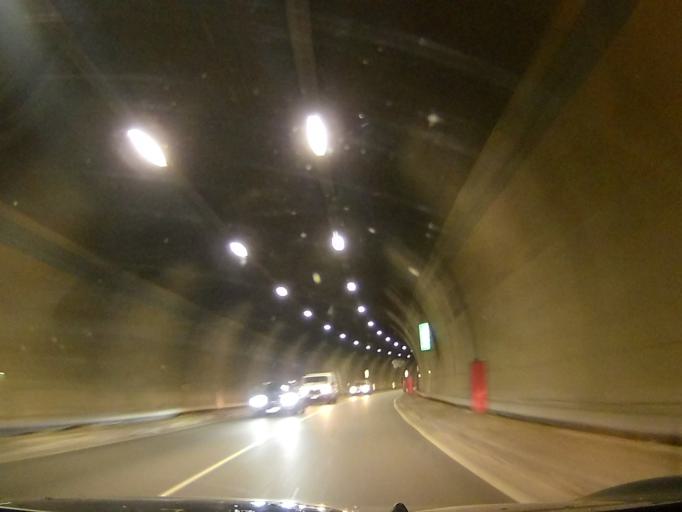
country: IT
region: Lombardy
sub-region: Provincia di Sondrio
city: Verceia
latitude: 46.1941
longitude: 9.4507
